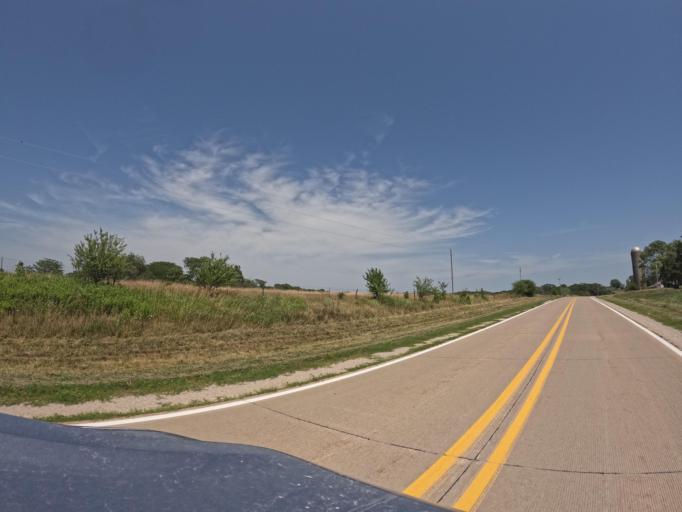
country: US
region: Iowa
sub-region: Henry County
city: Mount Pleasant
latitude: 40.9878
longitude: -91.6490
